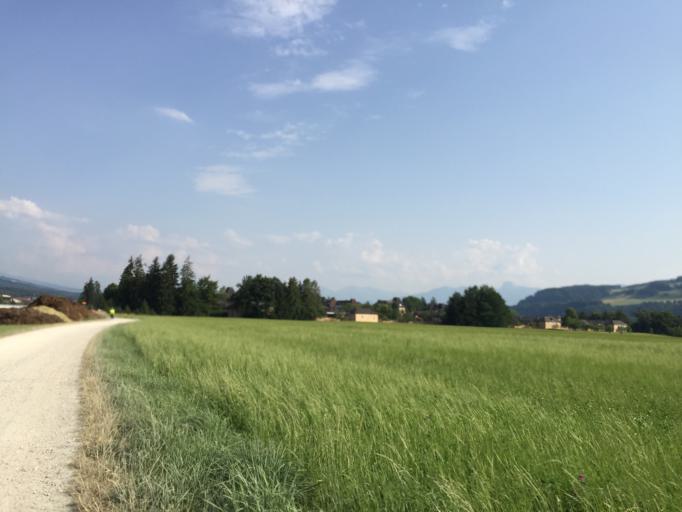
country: CH
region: Bern
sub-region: Bern-Mittelland District
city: Rubigen
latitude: 46.8853
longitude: 7.5508
